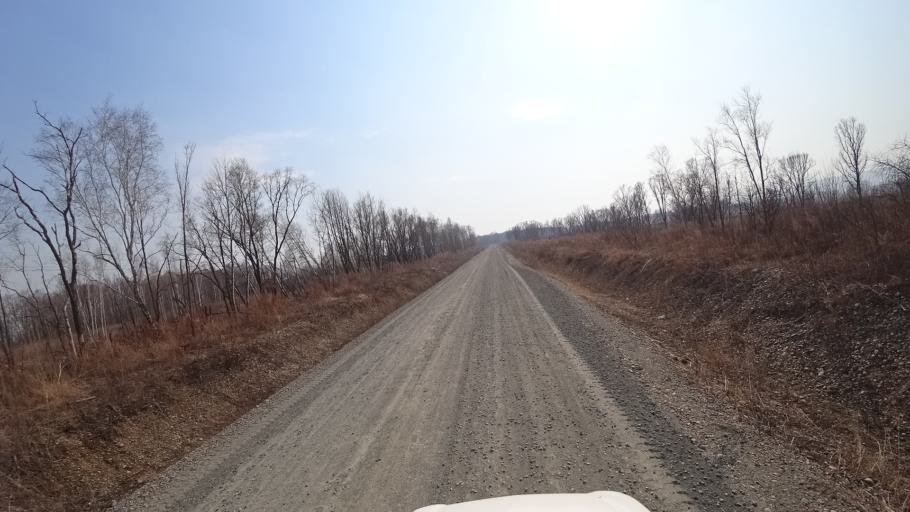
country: RU
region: Amur
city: Novobureyskiy
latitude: 49.8275
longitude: 129.9885
